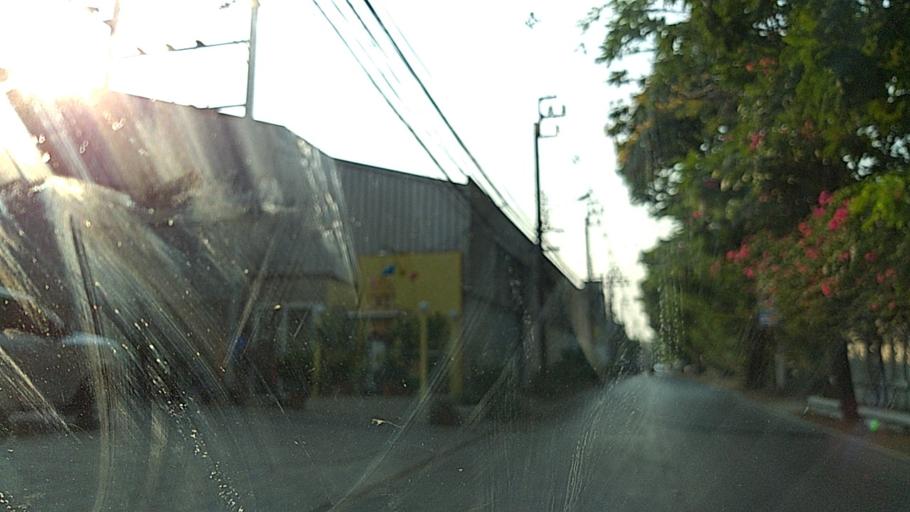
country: TH
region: Bangkok
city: Don Mueang
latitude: 13.9369
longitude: 100.5522
